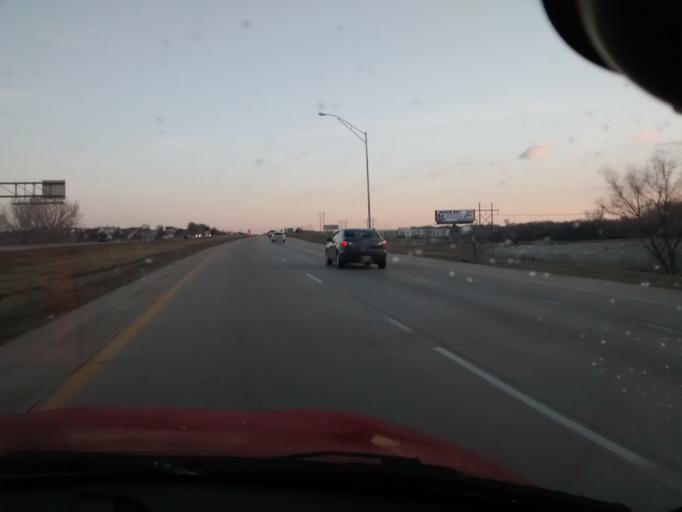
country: US
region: Nebraska
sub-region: Sarpy County
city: Offutt Air Force Base
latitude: 41.1452
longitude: -95.9386
